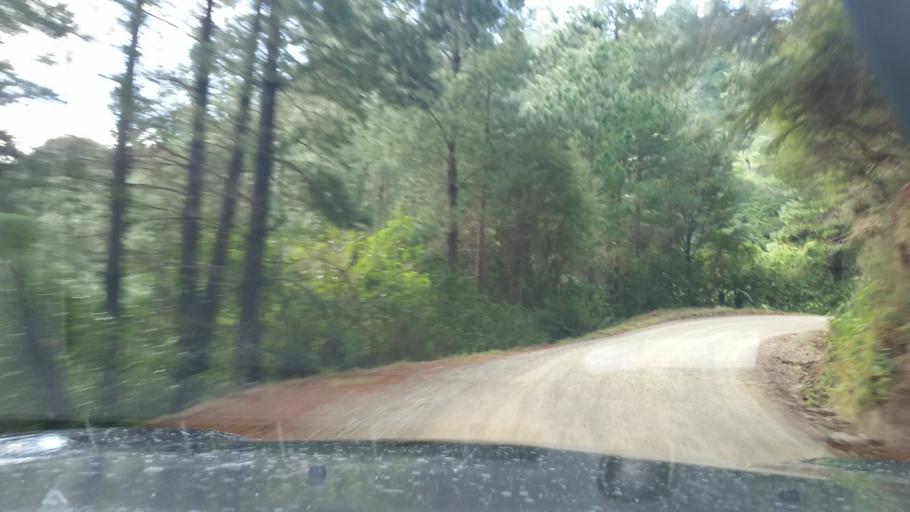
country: NZ
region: Marlborough
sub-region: Marlborough District
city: Picton
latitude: -41.1373
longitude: 174.1424
